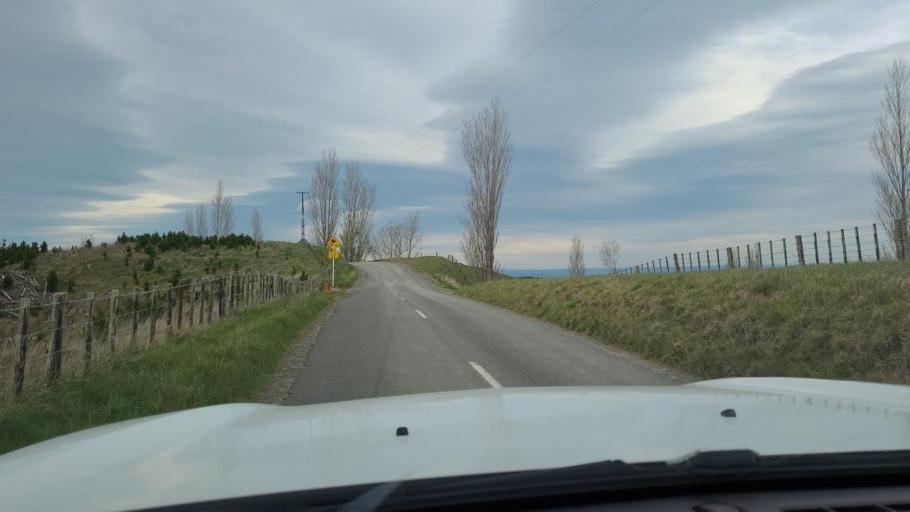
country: NZ
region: Hawke's Bay
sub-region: Napier City
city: Napier
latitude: -39.3485
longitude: 176.8258
